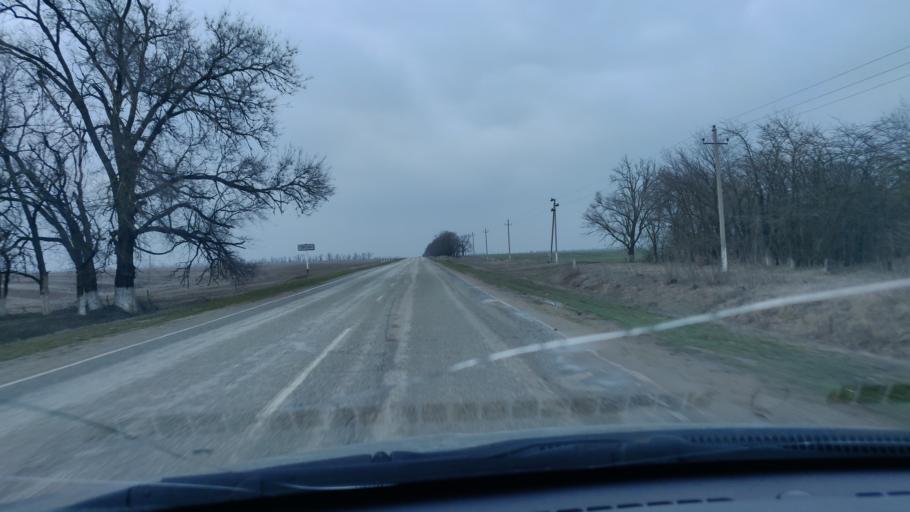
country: RU
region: Stavropol'skiy
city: Letnyaya Stavka
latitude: 45.3802
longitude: 43.3308
